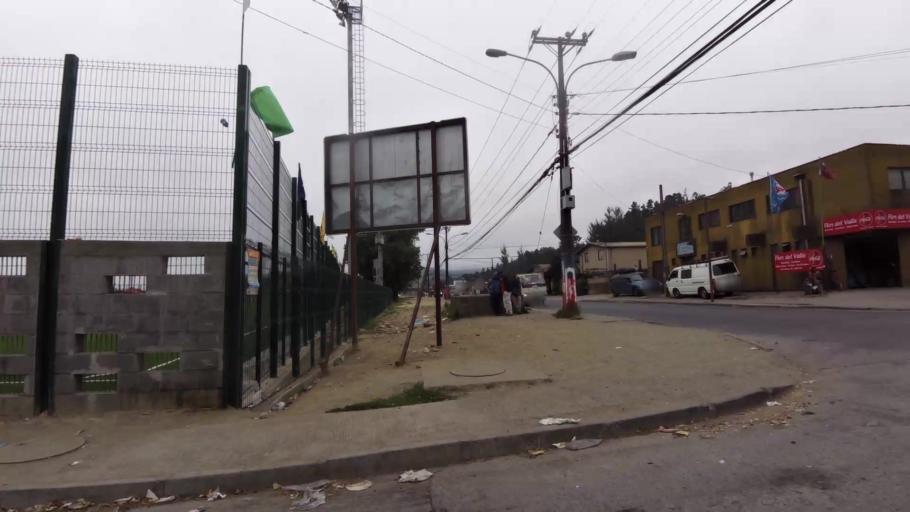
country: CL
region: Biobio
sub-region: Provincia de Concepcion
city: Concepcion
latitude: -36.8322
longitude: -73.0057
